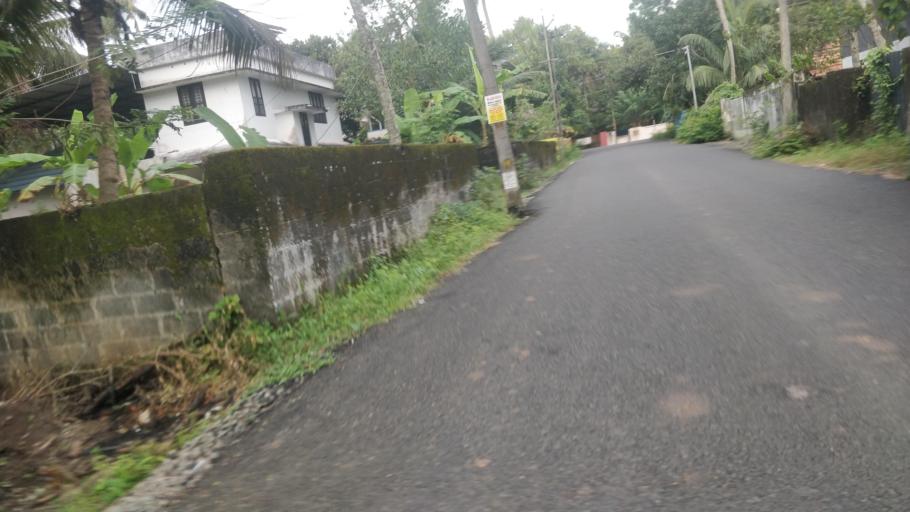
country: IN
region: Kerala
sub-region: Alappuzha
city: Shertallai
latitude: 9.6781
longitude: 76.3502
